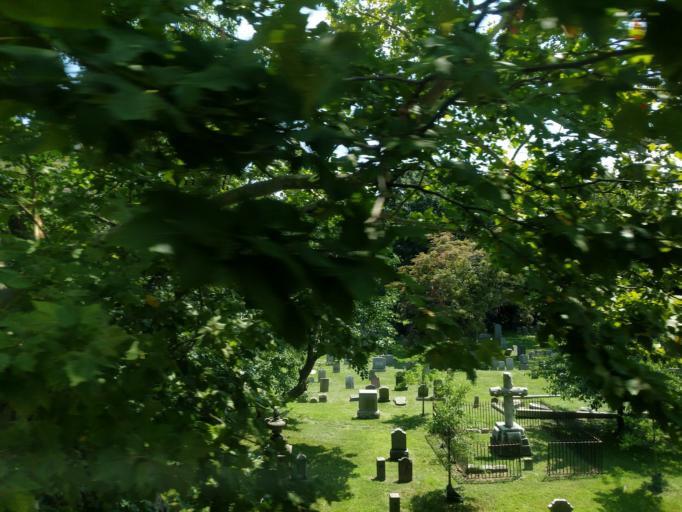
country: US
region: New York
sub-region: Bronx
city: The Bronx
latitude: 40.8385
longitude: -73.8444
